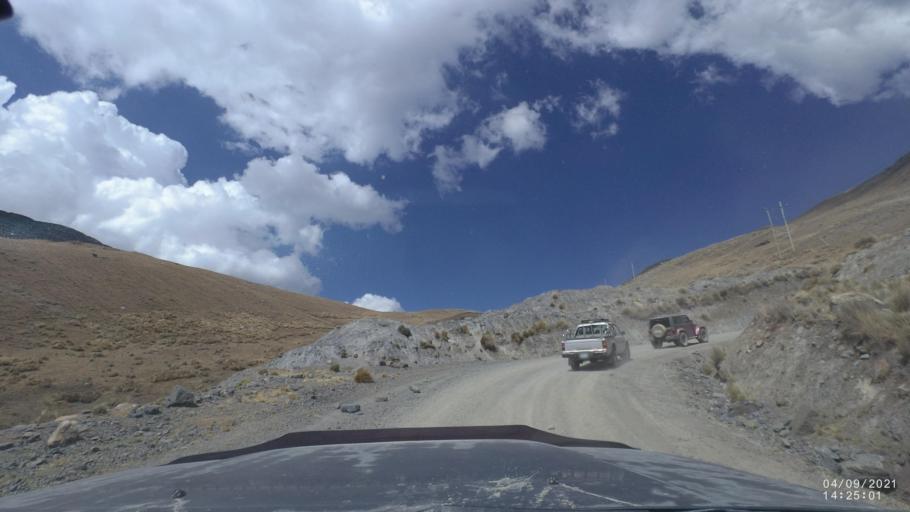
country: BO
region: Cochabamba
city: Sipe Sipe
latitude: -17.2423
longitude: -66.4069
